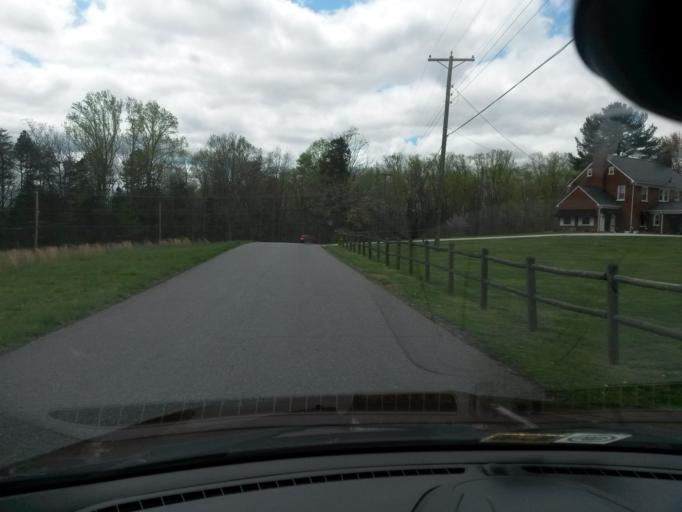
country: US
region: Virginia
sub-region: City of Lynchburg
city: West Lynchburg
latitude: 37.4028
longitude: -79.1944
